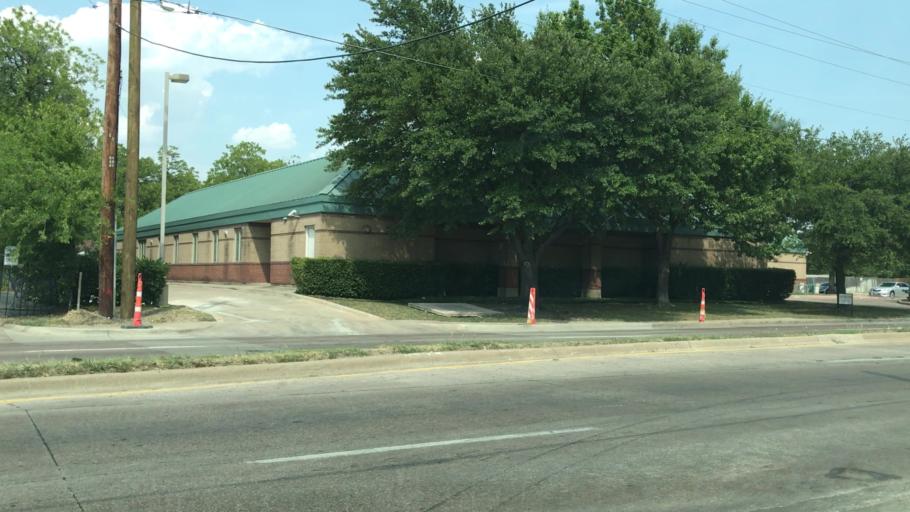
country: US
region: Texas
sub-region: Dallas County
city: University Park
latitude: 32.8644
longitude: -96.8620
